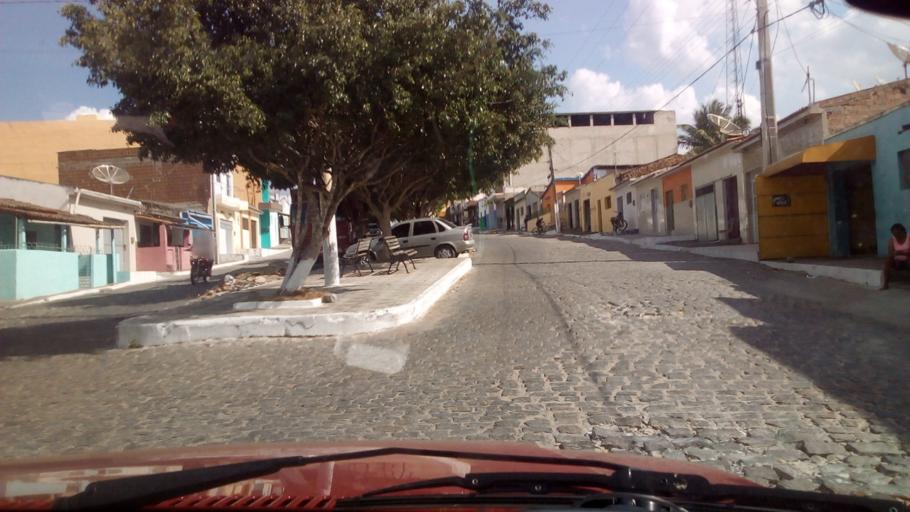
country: BR
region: Paraiba
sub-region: Arara
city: Arara
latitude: -6.8276
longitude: -35.7615
